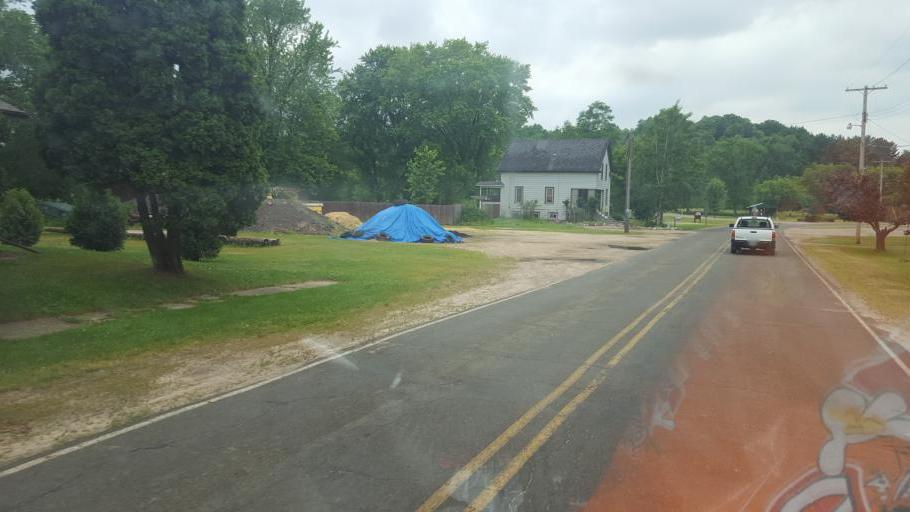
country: US
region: Wisconsin
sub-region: Juneau County
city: Elroy
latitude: 43.6530
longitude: -90.2247
